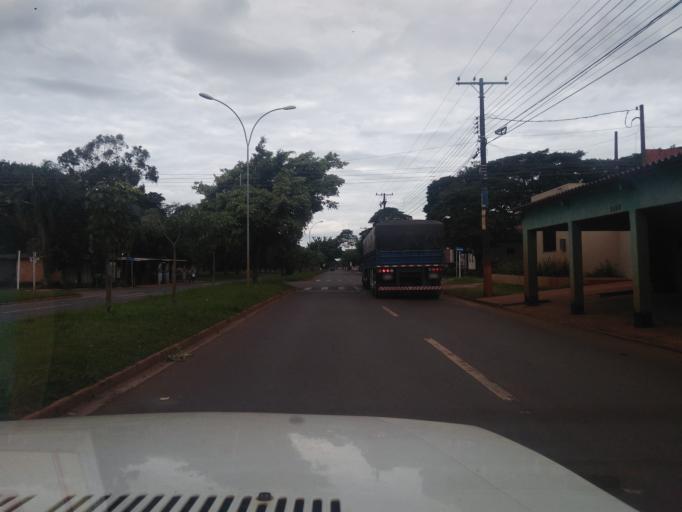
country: BR
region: Mato Grosso do Sul
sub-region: Ponta Pora
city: Ponta Pora
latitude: -22.5238
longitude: -55.7363
